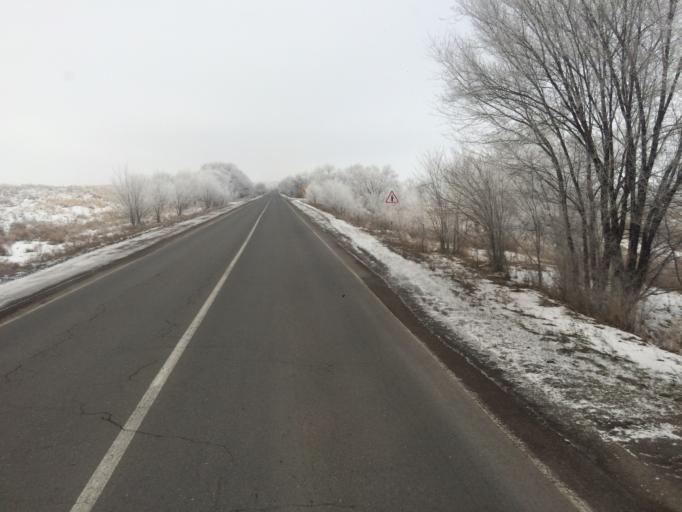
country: KG
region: Chuy
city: Bystrovka
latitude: 43.3232
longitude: 75.9223
